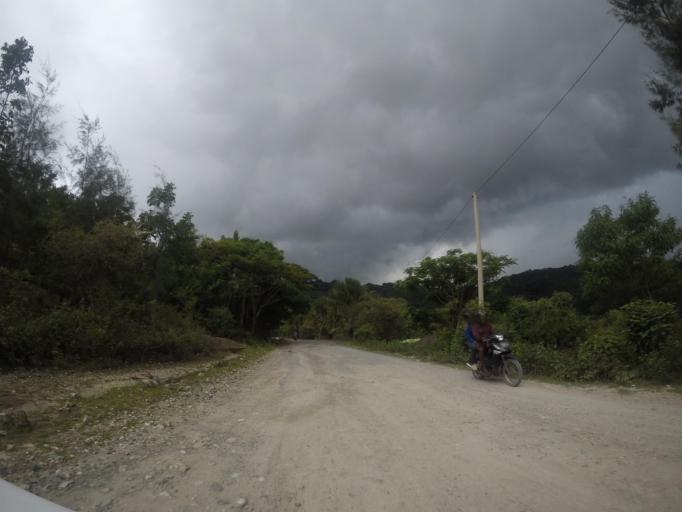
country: ID
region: East Nusa Tenggara
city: Atambua
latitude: -8.9647
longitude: 125.0249
